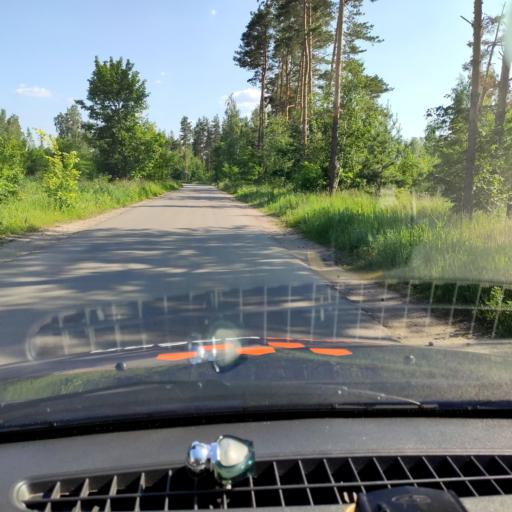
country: RU
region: Voronezj
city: Ramon'
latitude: 51.8914
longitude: 39.2067
